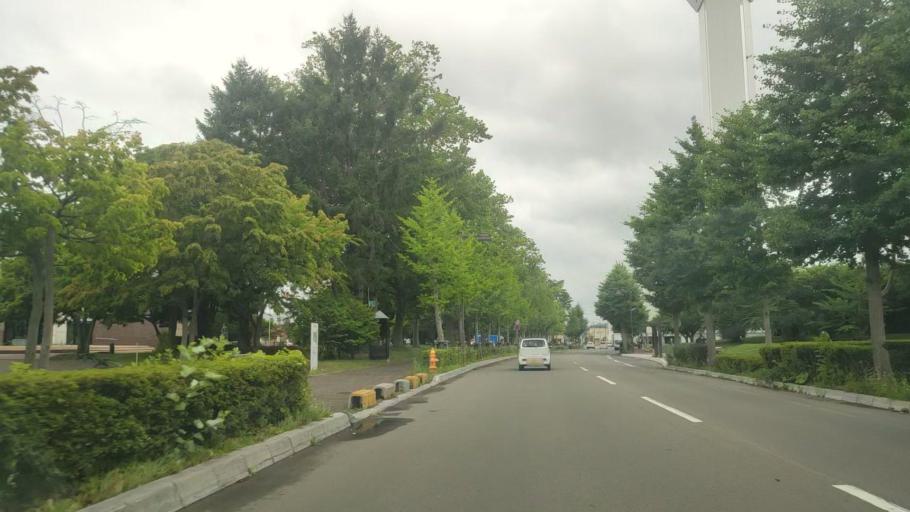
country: JP
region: Hokkaido
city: Hakodate
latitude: 41.7940
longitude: 140.7556
